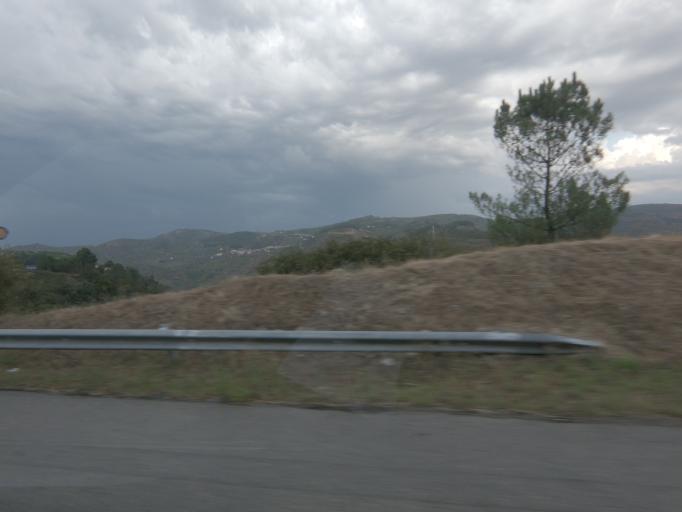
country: PT
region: Viseu
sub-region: Lamego
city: Lamego
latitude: 41.0949
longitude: -7.7829
